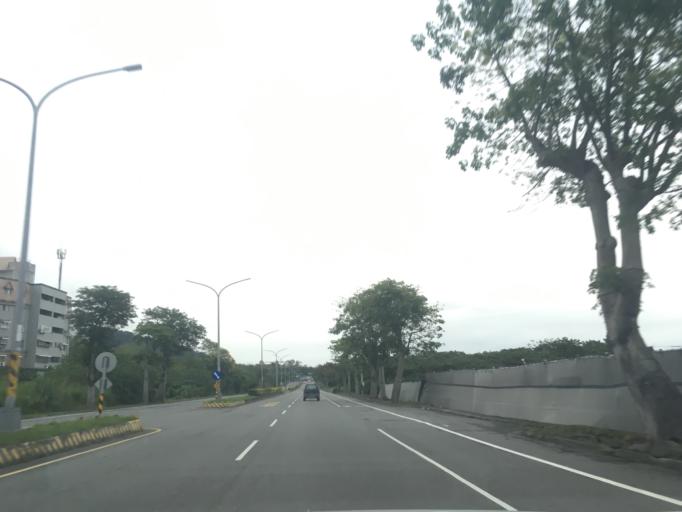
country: TW
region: Taiwan
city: Taitung City
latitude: 22.7081
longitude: 121.0428
